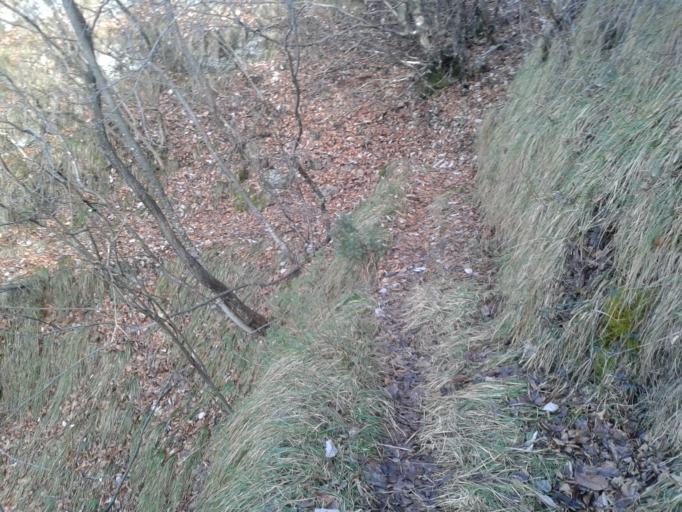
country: IT
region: Trentino-Alto Adige
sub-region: Provincia di Trento
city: Storo
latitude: 45.8343
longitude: 10.5712
